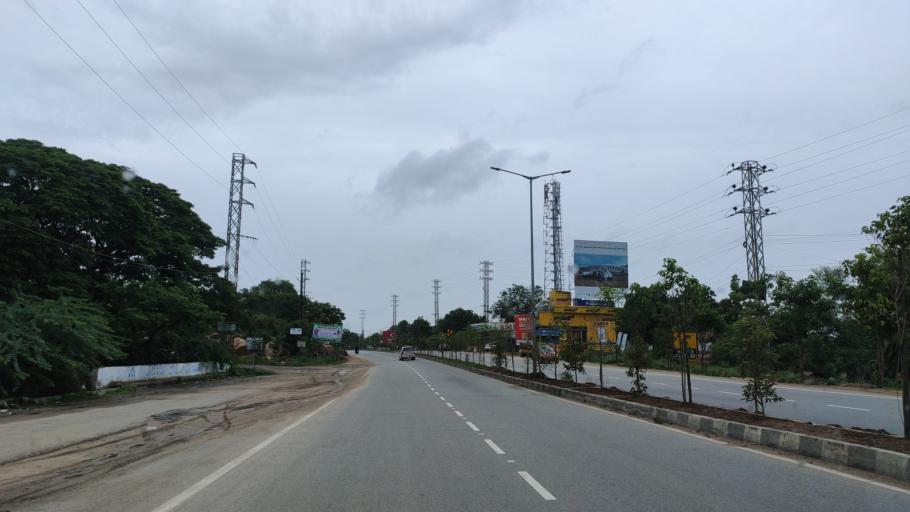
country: IN
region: Telangana
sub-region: Rangareddi
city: Secunderabad
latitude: 17.5964
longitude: 78.5689
